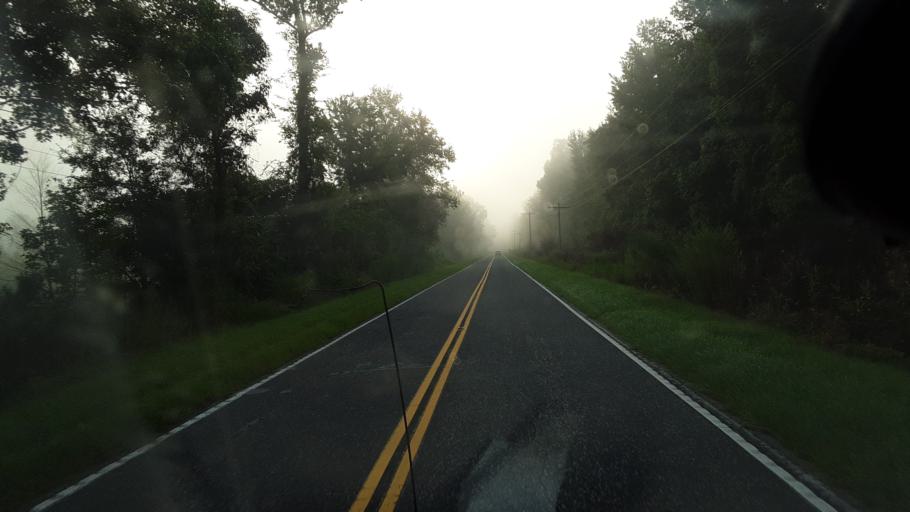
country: US
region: South Carolina
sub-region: Williamsburg County
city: Kingstree
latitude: 33.8236
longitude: -79.9615
